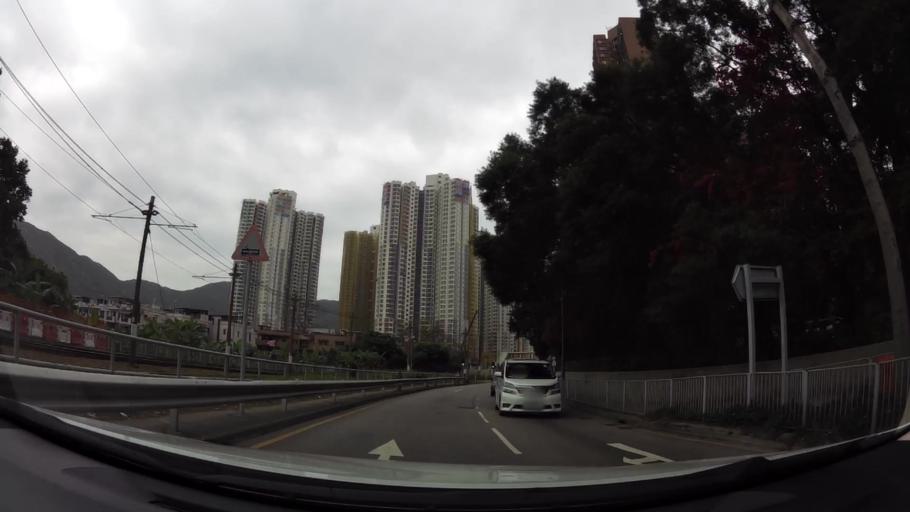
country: HK
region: Tuen Mun
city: Tuen Mun
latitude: 22.4117
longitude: 113.9765
